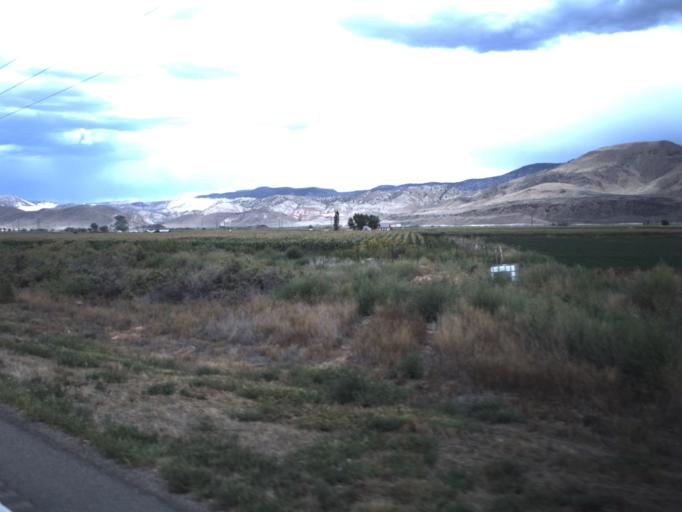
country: US
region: Utah
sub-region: Sevier County
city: Richfield
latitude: 38.8125
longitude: -112.0140
